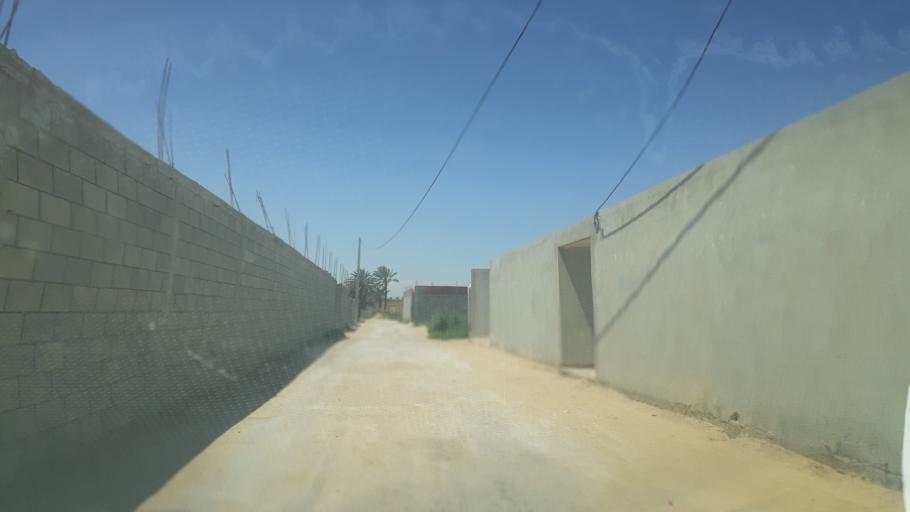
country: TN
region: Qabis
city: Gabes
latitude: 33.9341
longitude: 10.0593
